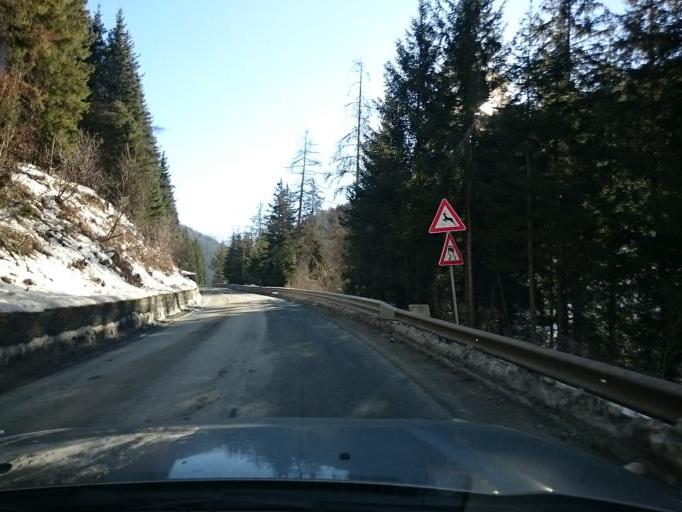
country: IT
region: Lombardy
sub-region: Provincia di Sondrio
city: Sant'Antonio
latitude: 46.4434
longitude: 10.4434
